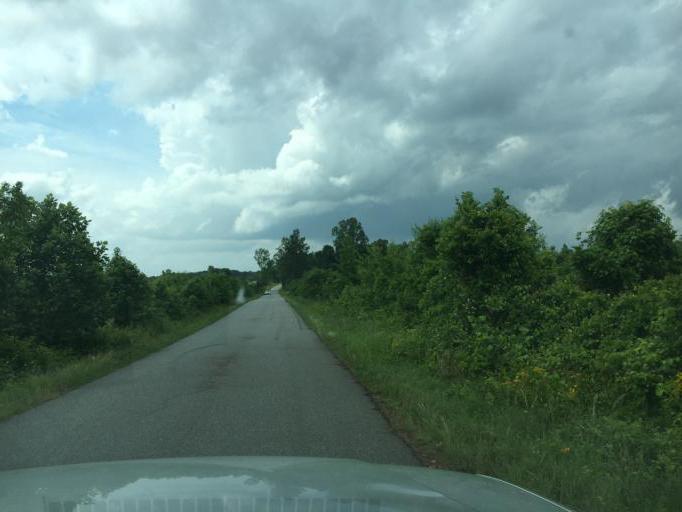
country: US
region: South Carolina
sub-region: Spartanburg County
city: Fairforest
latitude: 34.9246
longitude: -82.0538
